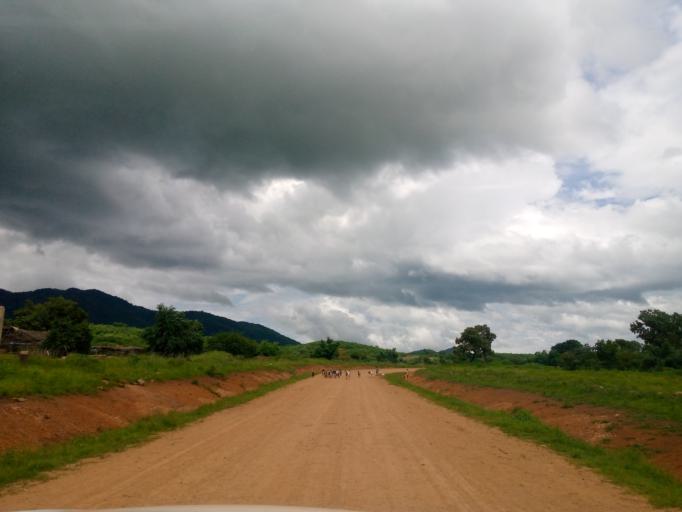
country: ET
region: Oromiya
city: Mendi
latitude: 10.2037
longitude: 35.0917
